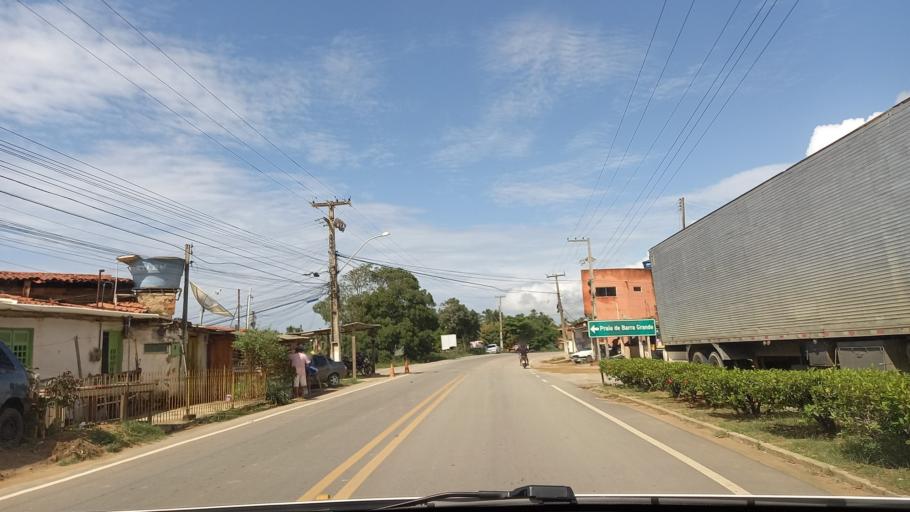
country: BR
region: Alagoas
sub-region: Maragogi
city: Maragogi
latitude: -8.9847
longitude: -35.1968
